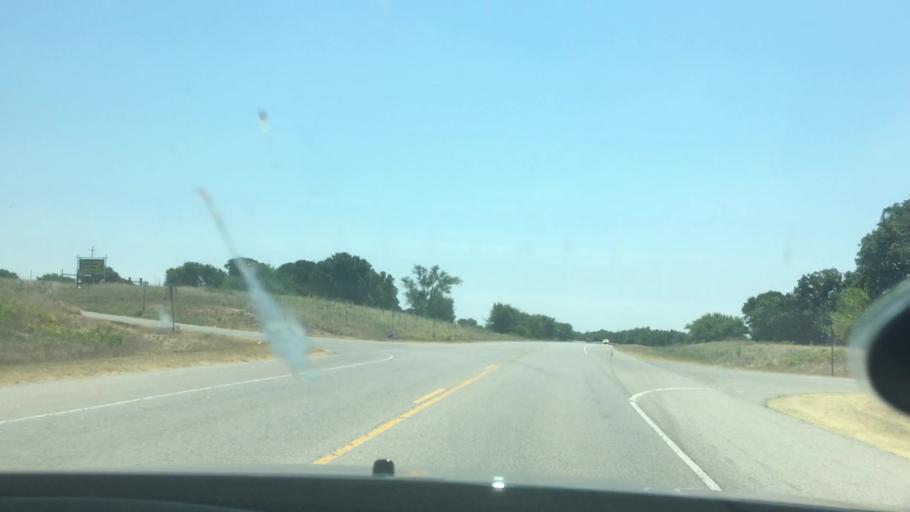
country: US
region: Oklahoma
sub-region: Pontotoc County
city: Ada
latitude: 34.6950
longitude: -96.5977
